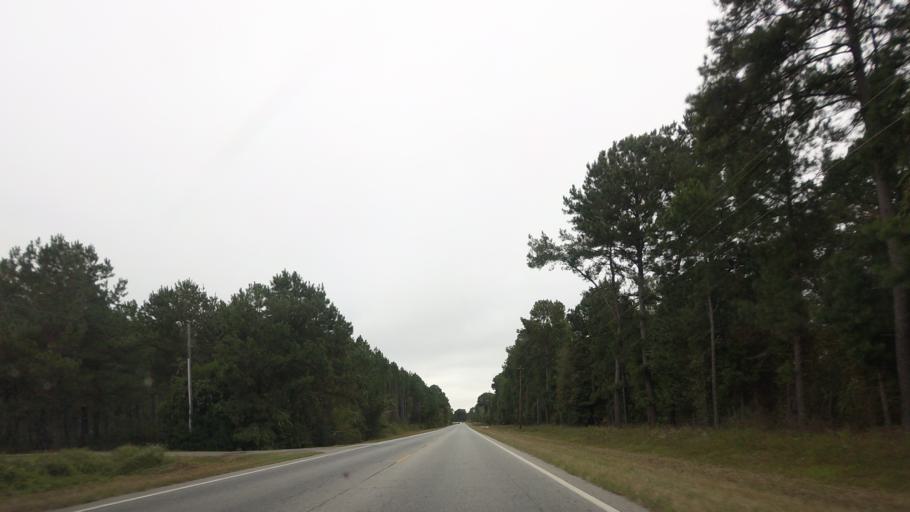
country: US
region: Georgia
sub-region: Berrien County
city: Ray City
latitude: 31.1366
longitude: -83.2161
